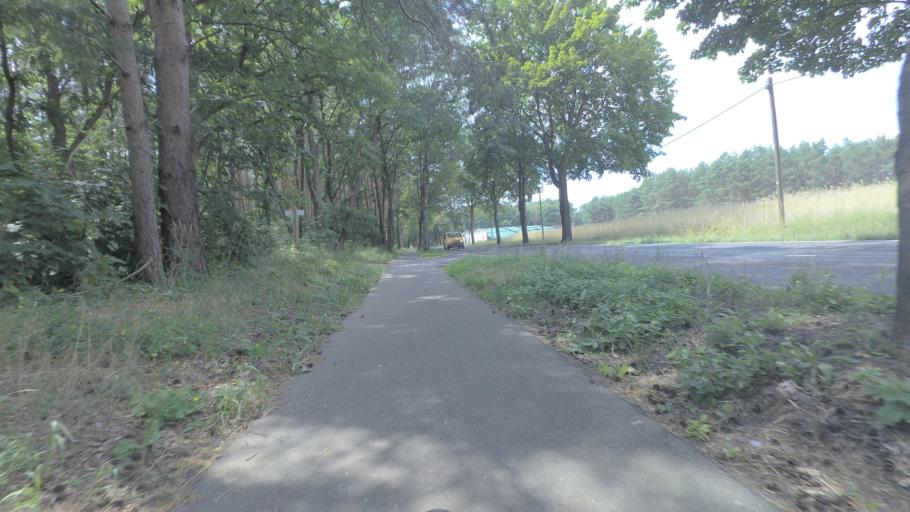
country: DE
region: Brandenburg
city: Luckenwalde
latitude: 52.1164
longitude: 13.2267
